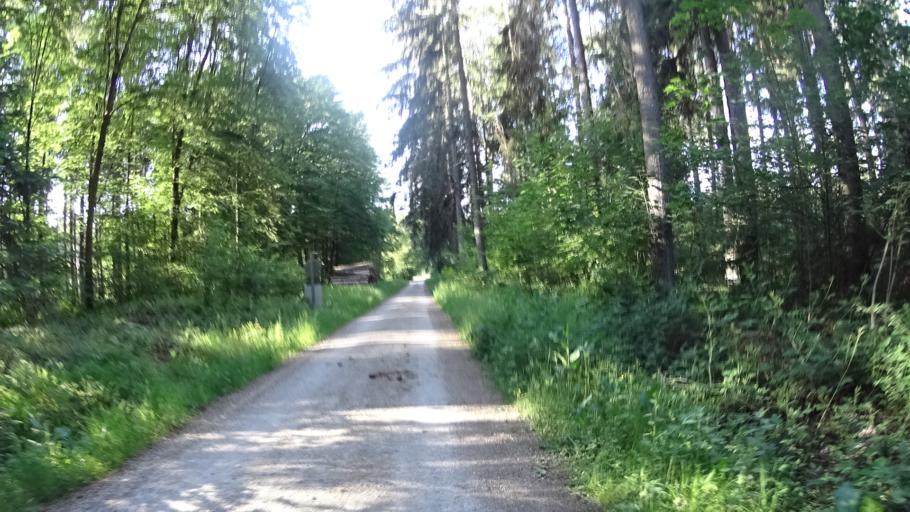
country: DE
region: Bavaria
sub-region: Regierungsbezirk Mittelfranken
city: Lichtenau
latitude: 49.1523
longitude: 10.3923
